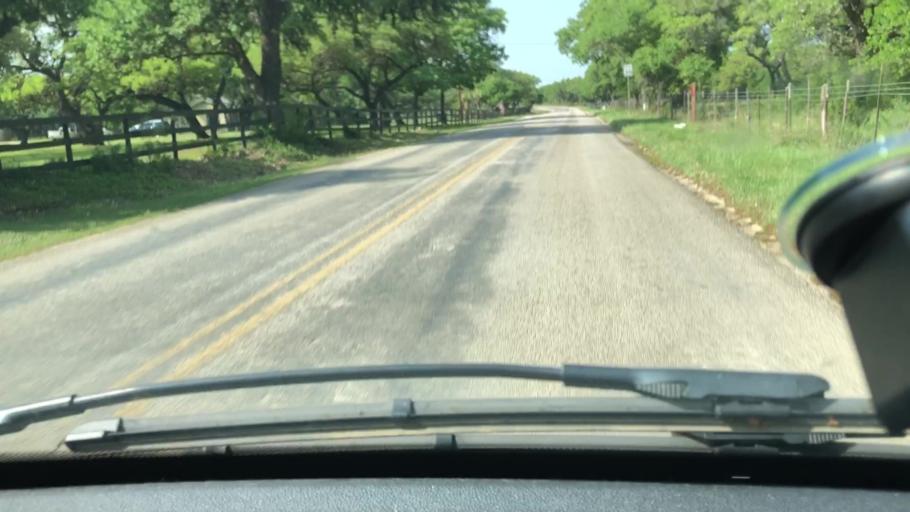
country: US
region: Texas
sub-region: Comal County
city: Bulverde
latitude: 29.7615
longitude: -98.4587
